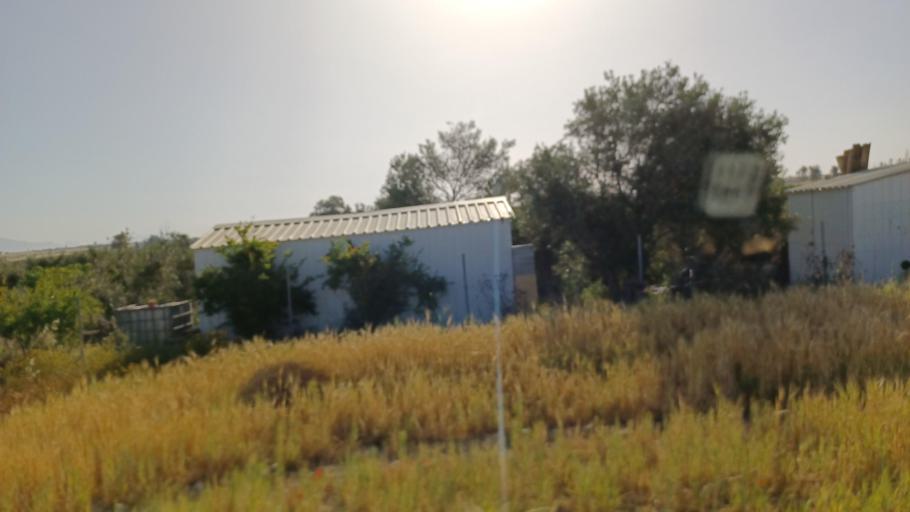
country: CY
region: Lefkosia
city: Mammari
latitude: 35.1607
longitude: 33.2474
